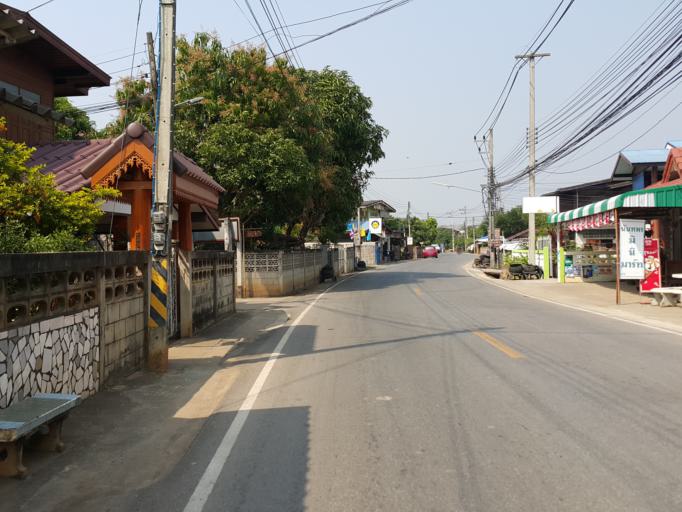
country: TH
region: Sukhothai
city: Thung Saliam
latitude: 17.3257
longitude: 99.5334
